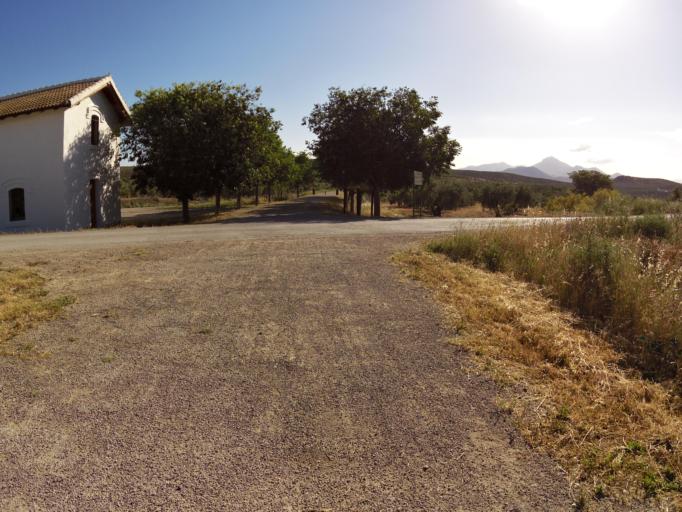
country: ES
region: Andalusia
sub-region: Province of Cordoba
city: Luque
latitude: 37.5811
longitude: -4.2144
